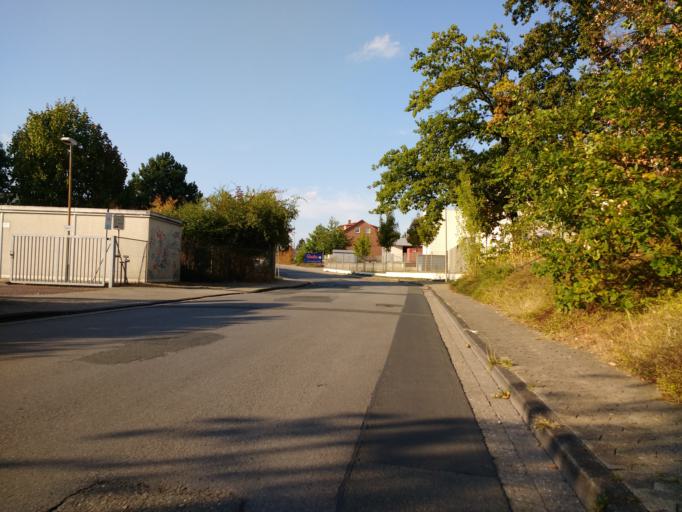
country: DE
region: Lower Saxony
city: Gifhorn
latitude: 52.4772
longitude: 10.5404
